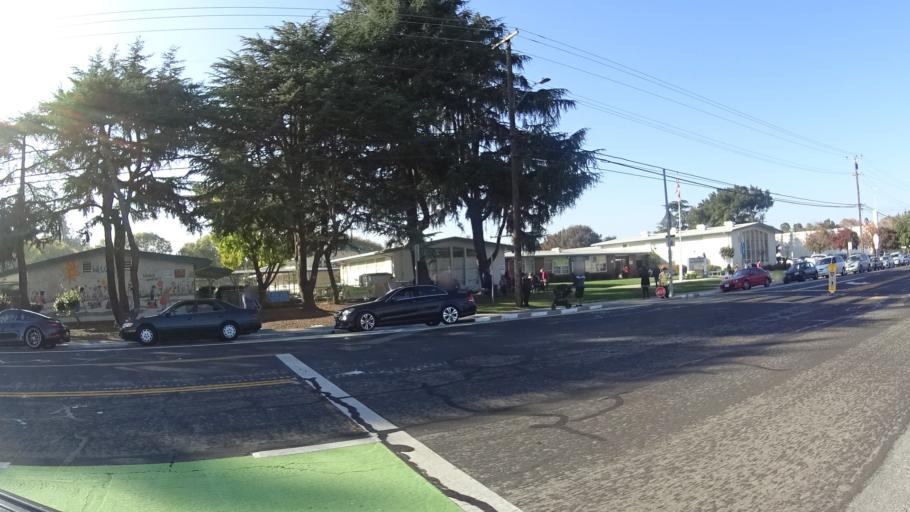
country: US
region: California
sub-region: Santa Clara County
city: Santa Clara
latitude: 37.3477
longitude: -121.9867
